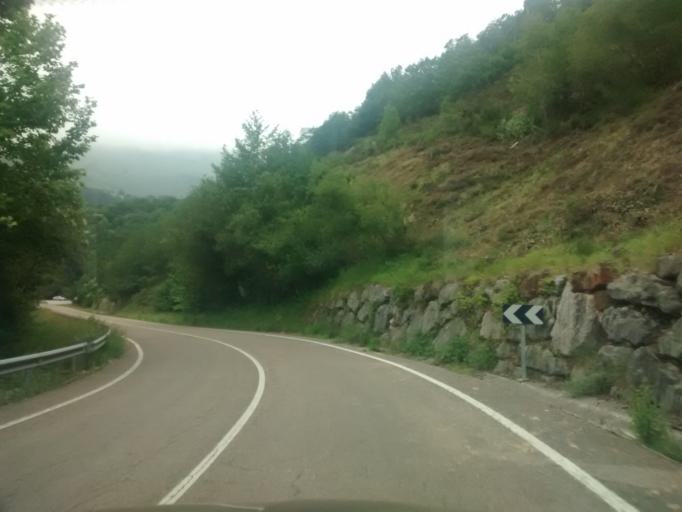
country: ES
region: Cantabria
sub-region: Provincia de Cantabria
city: Ruente
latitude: 43.1677
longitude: -4.2778
